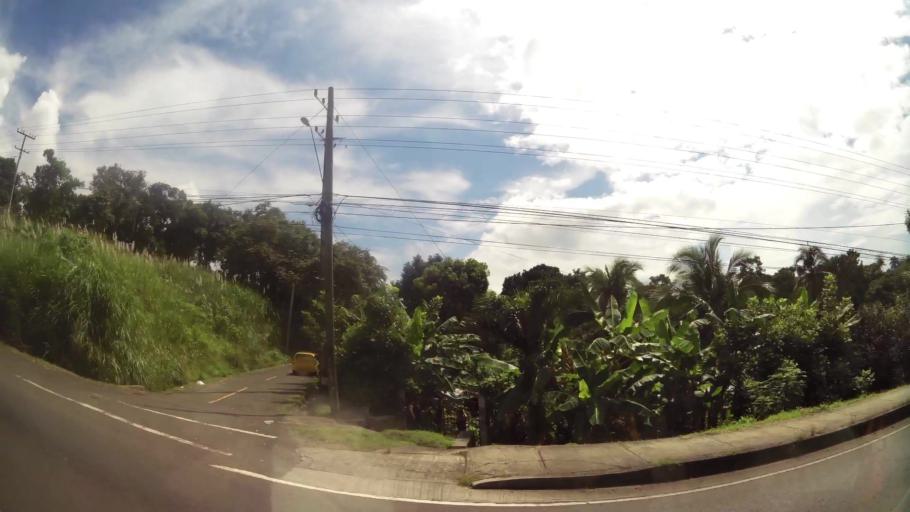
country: PA
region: Panama
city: Vista Alegre
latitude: 8.9381
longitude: -79.6838
